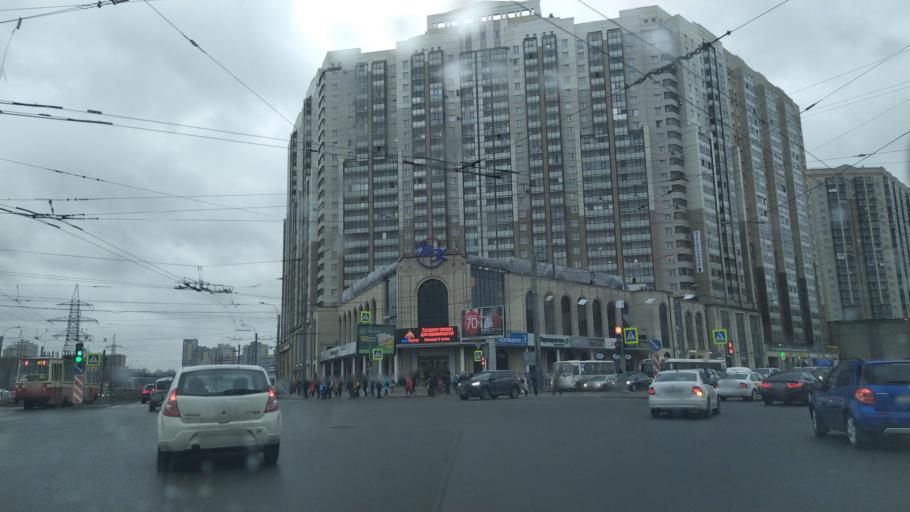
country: RU
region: Leningrad
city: Chernaya Rechka
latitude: 60.0029
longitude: 30.2976
